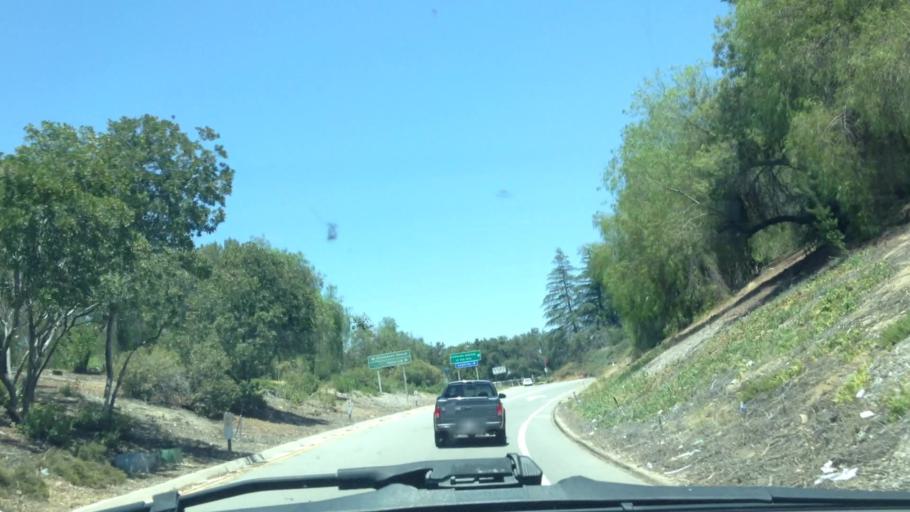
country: US
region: California
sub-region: Los Angeles County
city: Santa Clarita
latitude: 34.3926
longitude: -118.5703
